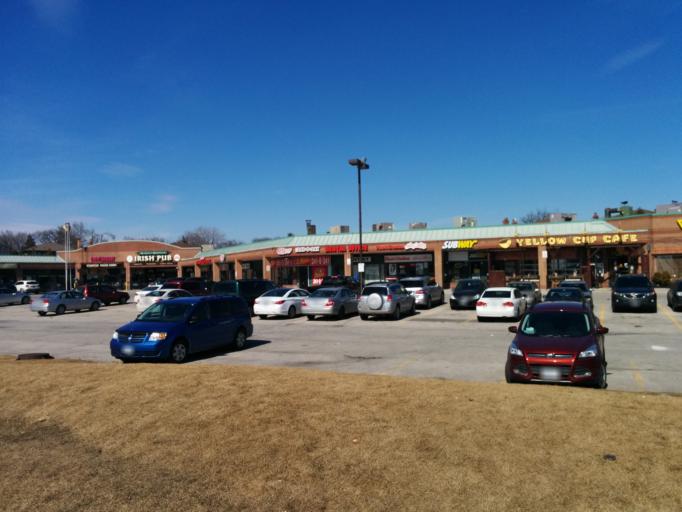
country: CA
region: Ontario
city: Etobicoke
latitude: 43.6316
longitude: -79.5522
